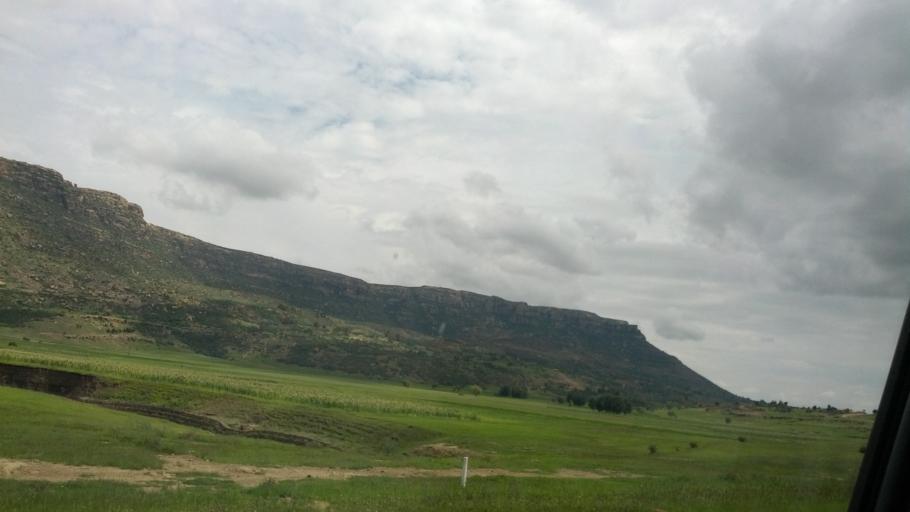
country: LS
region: Maseru
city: Maseru
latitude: -29.5218
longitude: 27.5230
